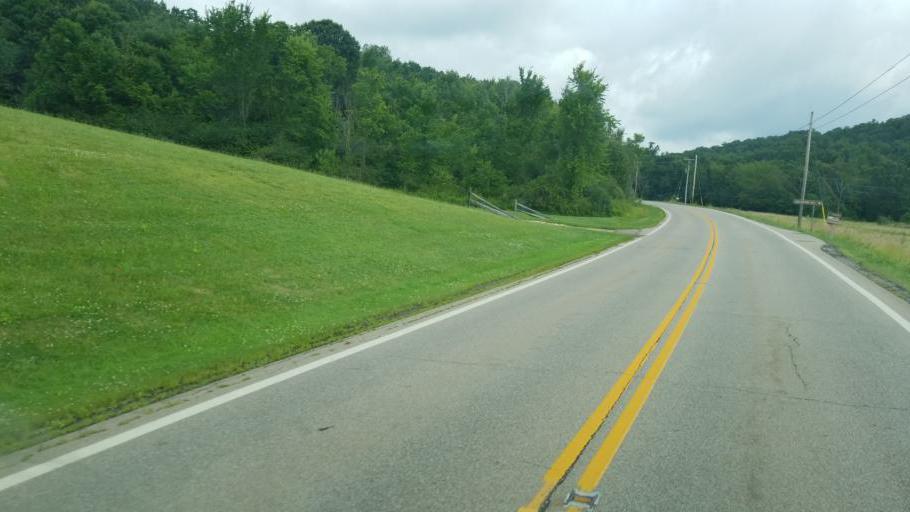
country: US
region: Ohio
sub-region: Columbiana County
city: Salineville
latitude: 40.6666
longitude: -80.8057
